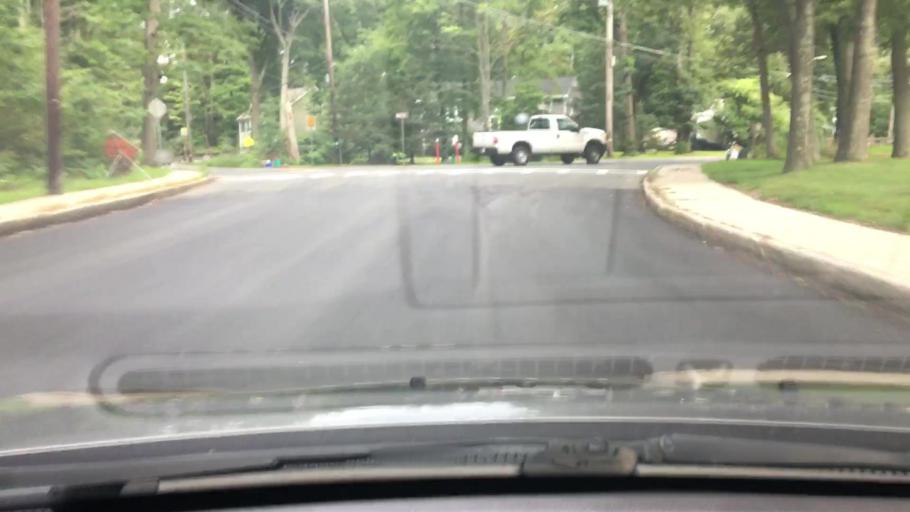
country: US
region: Massachusetts
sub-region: Worcester County
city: Hopedale
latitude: 42.1588
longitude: -71.5374
